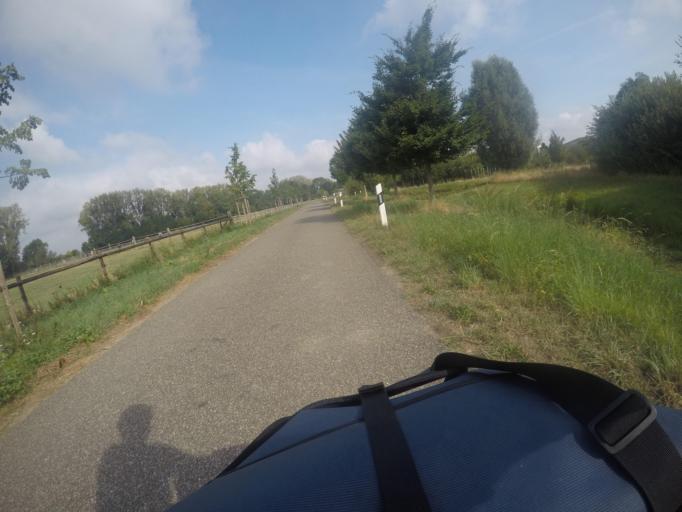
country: DE
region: North Rhine-Westphalia
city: Geldern
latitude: 51.5101
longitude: 6.3158
